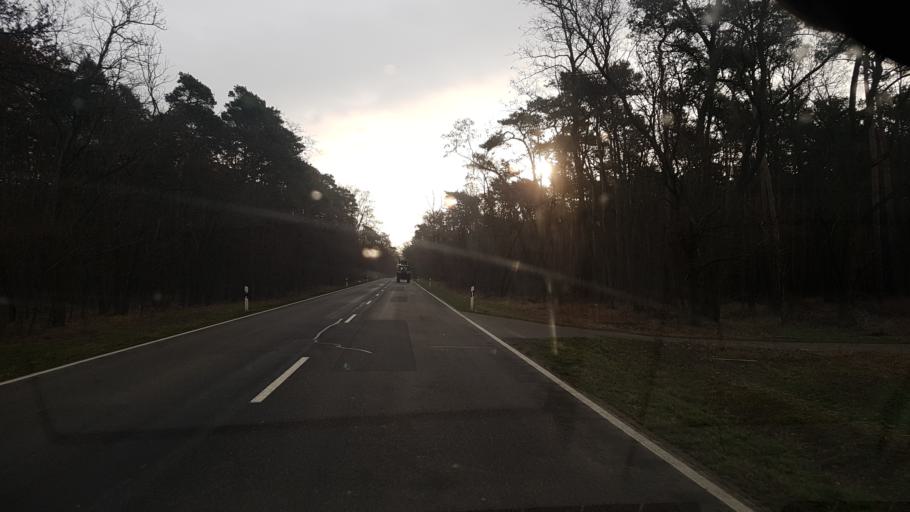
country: DE
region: Brandenburg
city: Werben
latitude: 51.7573
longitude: 14.1680
